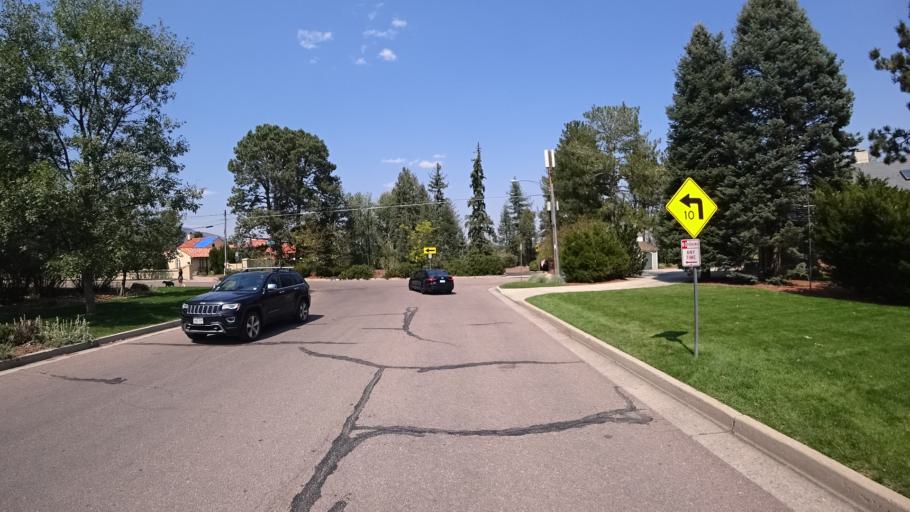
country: US
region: Colorado
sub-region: El Paso County
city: Colorado Springs
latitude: 38.7964
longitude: -104.8451
